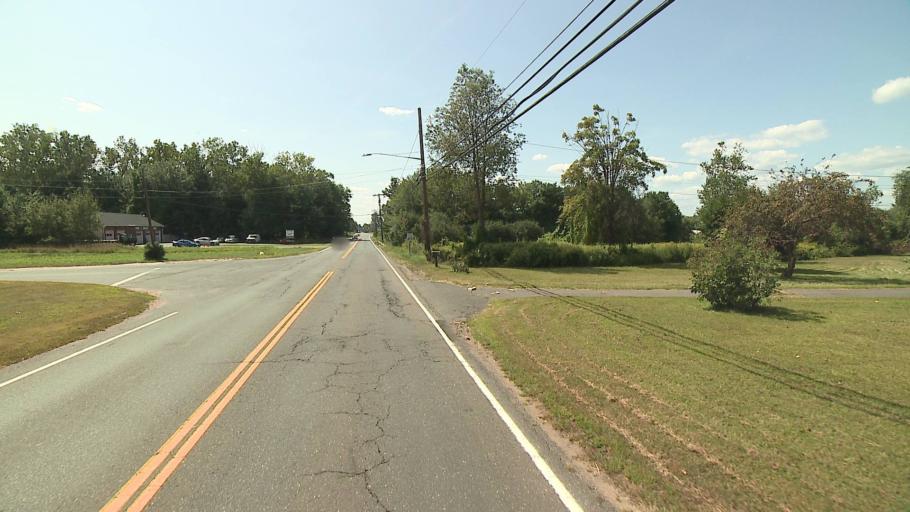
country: US
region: Connecticut
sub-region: Hartford County
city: Southwood Acres
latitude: 41.9373
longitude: -72.5725
